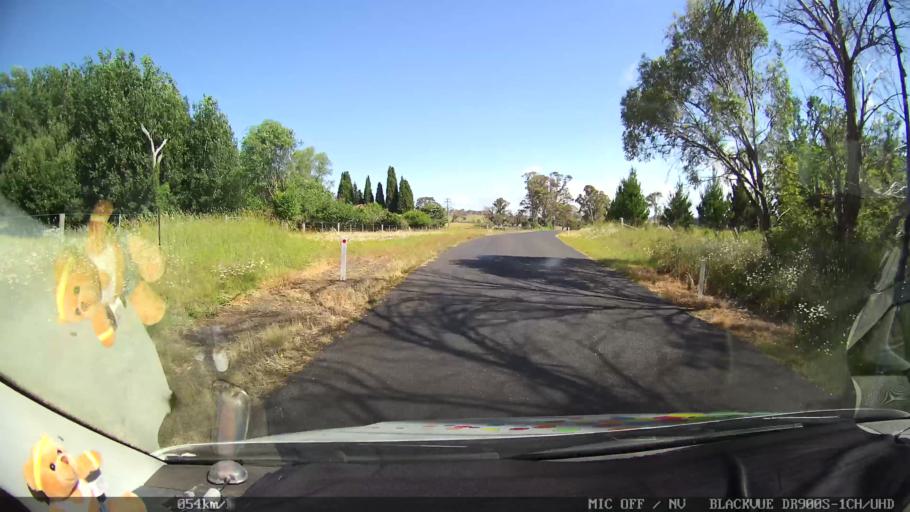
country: AU
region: New South Wales
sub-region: Guyra
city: Guyra
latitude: -30.1032
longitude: 151.6784
